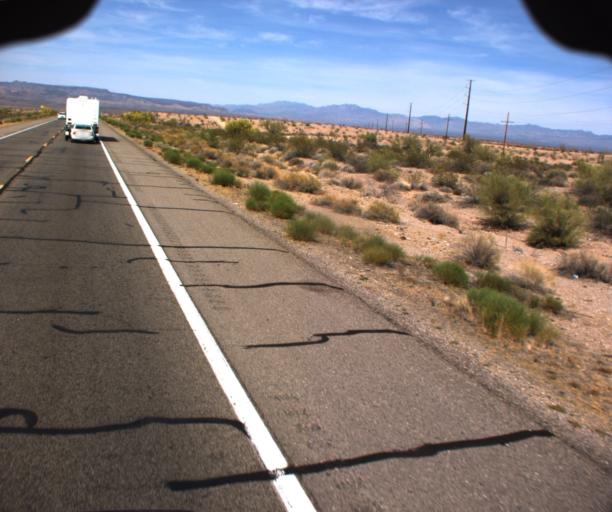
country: US
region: Arizona
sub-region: Mohave County
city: Desert Hills
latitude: 34.6658
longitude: -114.3128
